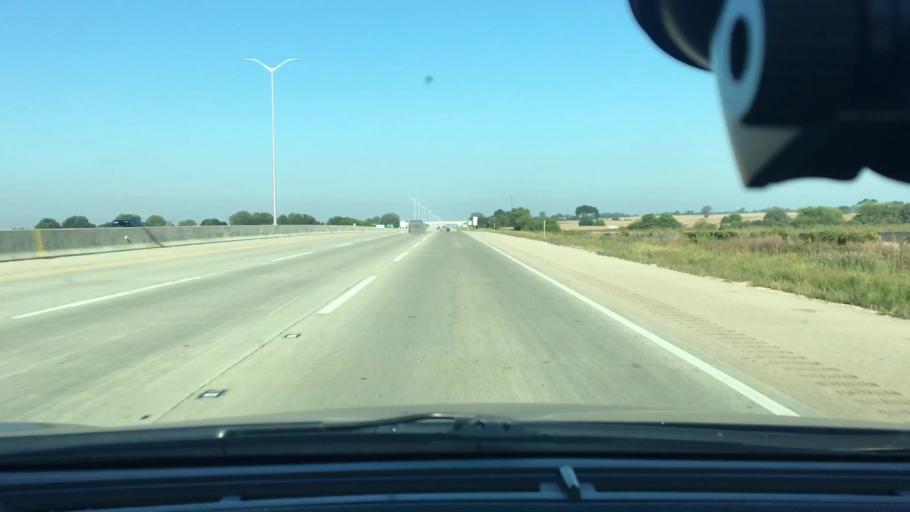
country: US
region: Illinois
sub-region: Kane County
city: Hampshire
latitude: 42.1473
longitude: -88.5218
